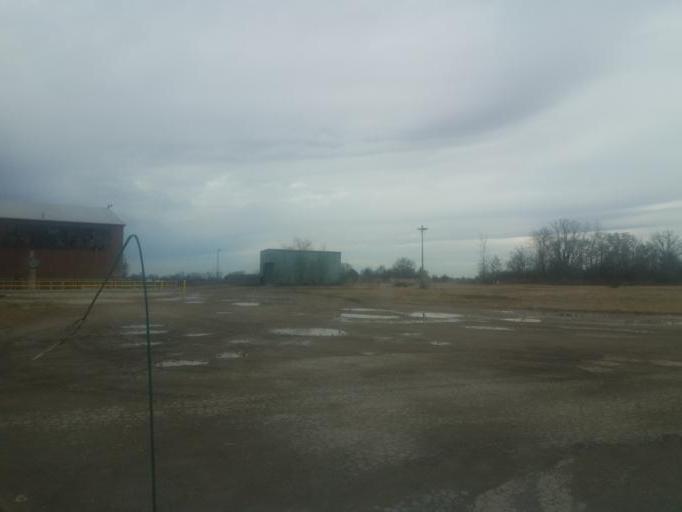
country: US
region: Ohio
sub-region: Marion County
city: Marion
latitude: 40.5939
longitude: -83.1045
